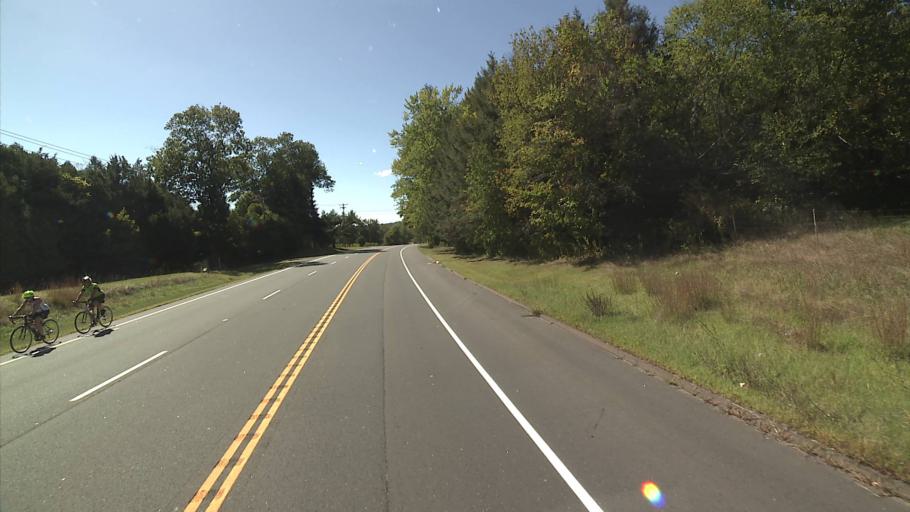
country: US
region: Connecticut
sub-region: New Haven County
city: Woodbridge
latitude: 41.3681
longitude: -72.9806
